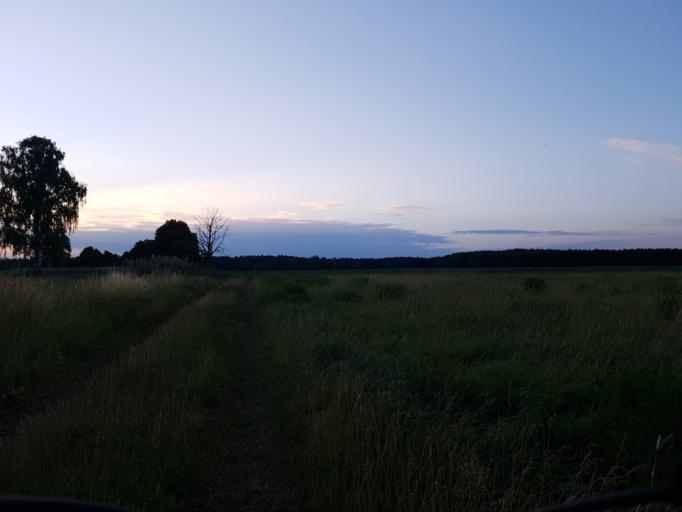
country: DE
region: Brandenburg
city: Schilda
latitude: 51.5765
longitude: 13.3526
